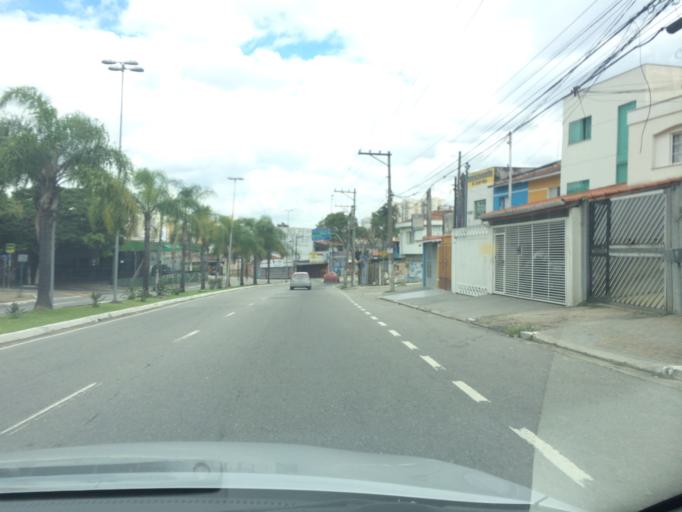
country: BR
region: Sao Paulo
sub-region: Guarulhos
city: Guarulhos
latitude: -23.4561
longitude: -46.5201
